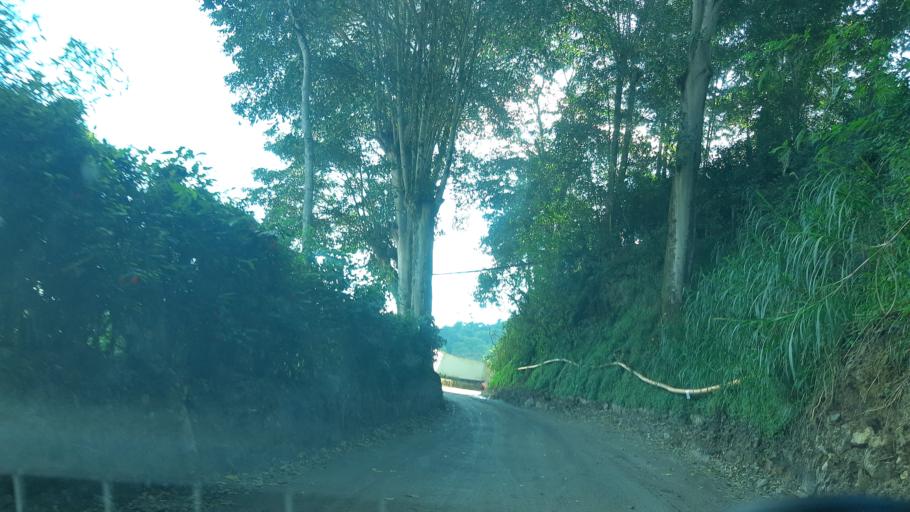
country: CO
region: Boyaca
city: Garagoa
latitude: 5.0874
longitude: -73.3827
